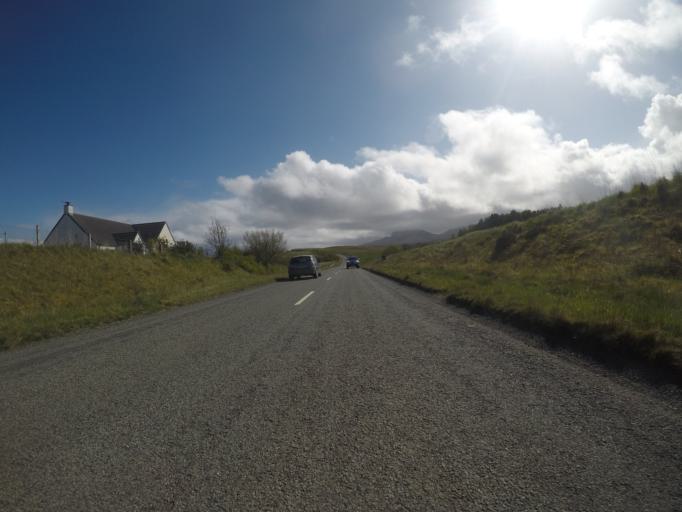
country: GB
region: Scotland
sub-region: Highland
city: Portree
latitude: 57.5819
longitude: -6.1578
